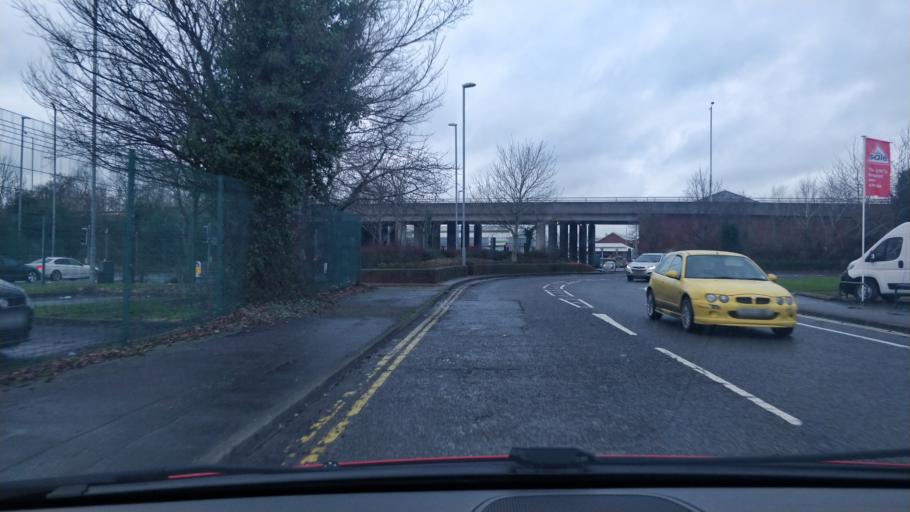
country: GB
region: England
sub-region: Lancashire
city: Preston
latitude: 53.7580
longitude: -2.7182
